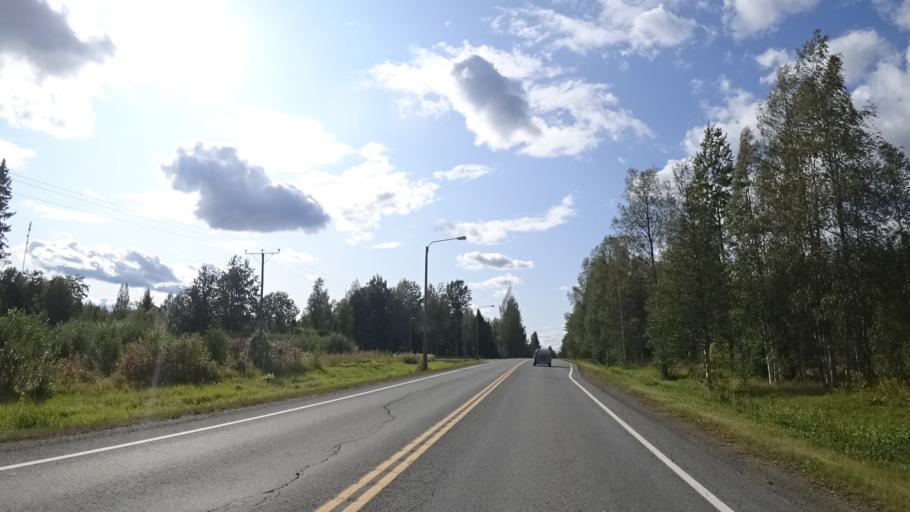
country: FI
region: North Karelia
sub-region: Keski-Karjala
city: Tohmajaervi
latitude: 62.2221
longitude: 30.3572
